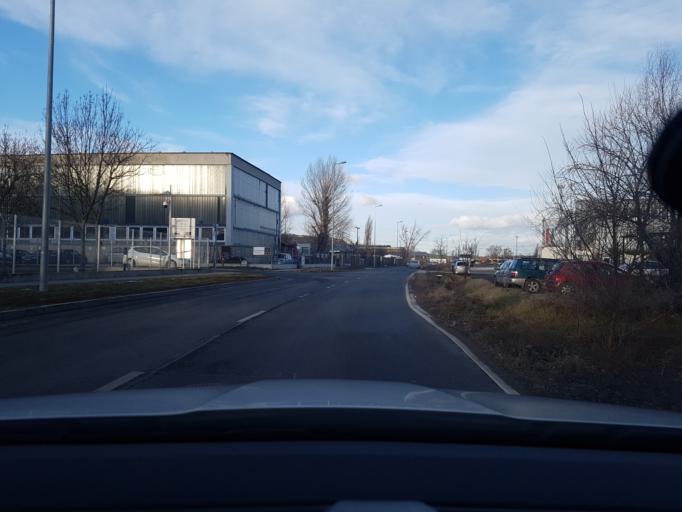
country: HU
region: Budapest
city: Budapest III. keruelet
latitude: 47.5653
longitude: 19.0309
